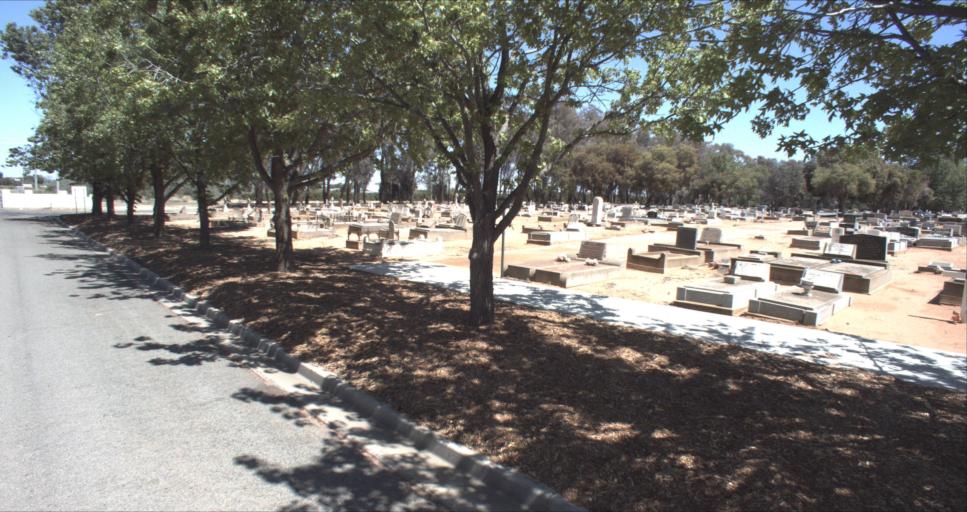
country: AU
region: New South Wales
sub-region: Leeton
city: Leeton
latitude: -34.5324
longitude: 146.3991
